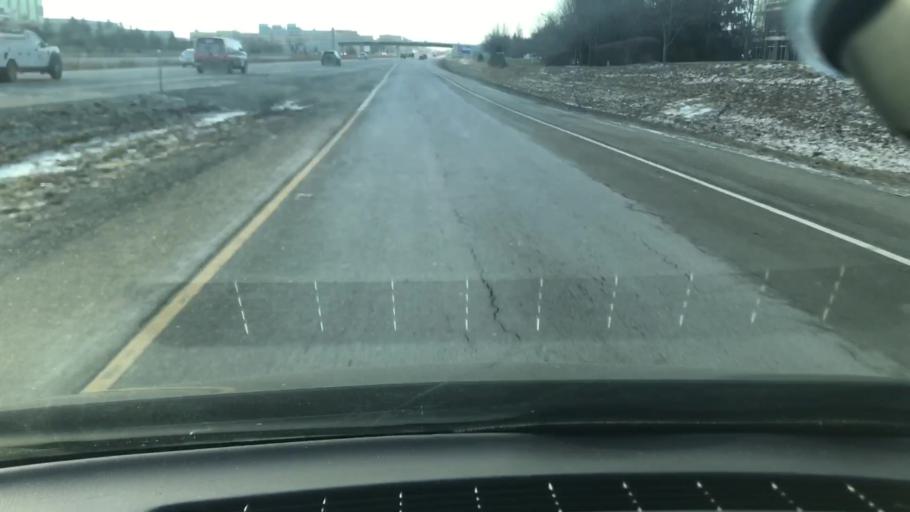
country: US
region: Indiana
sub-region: Hamilton County
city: Carmel
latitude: 39.9756
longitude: -86.1582
